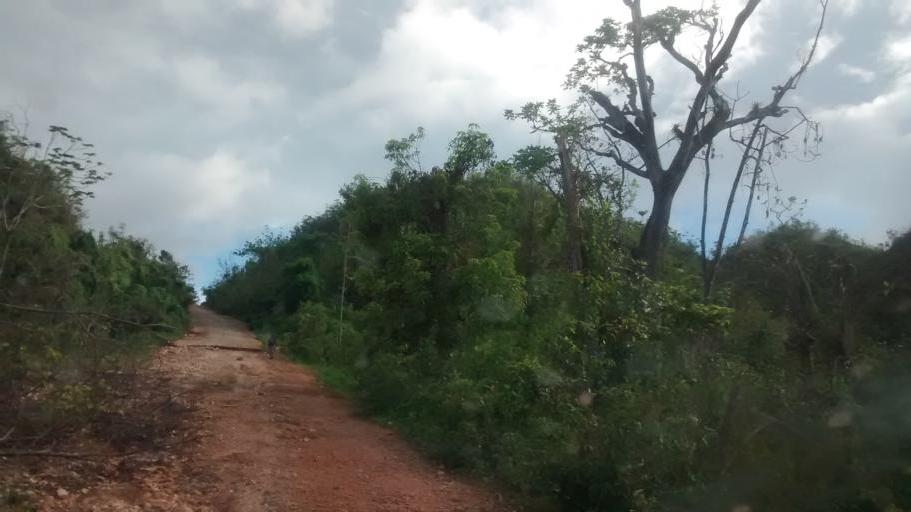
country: HT
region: Grandans
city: Corail
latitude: 18.5093
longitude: -73.7828
